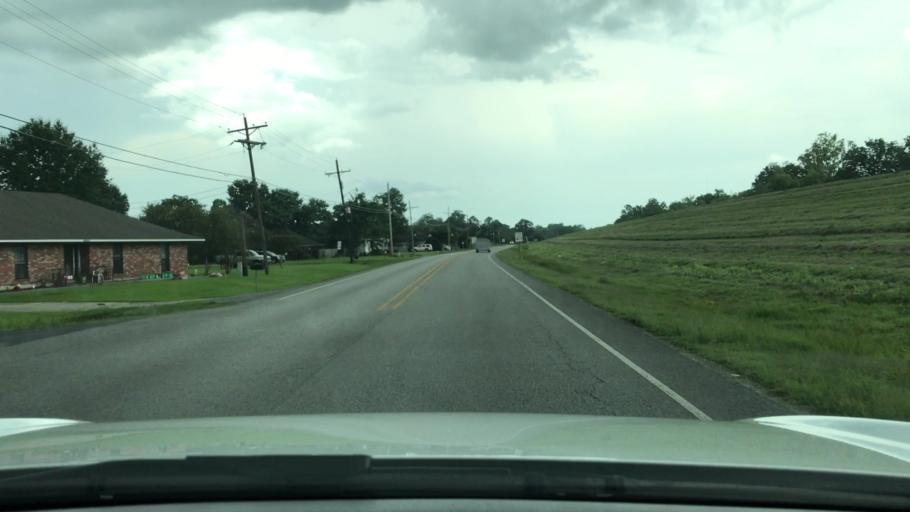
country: US
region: Louisiana
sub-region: Iberville Parish
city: Plaquemine
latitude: 30.2782
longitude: -91.2169
